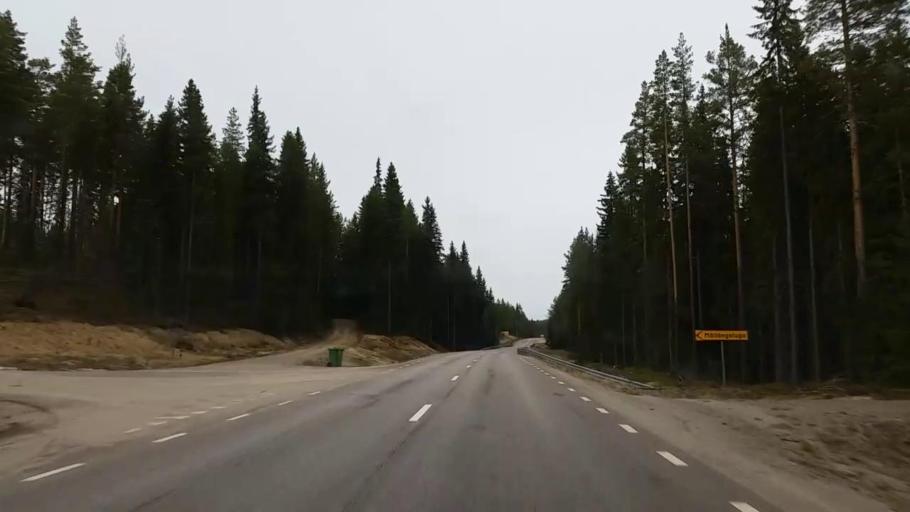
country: SE
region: Gaevleborg
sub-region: Ovanakers Kommun
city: Edsbyn
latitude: 61.1673
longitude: 15.8826
